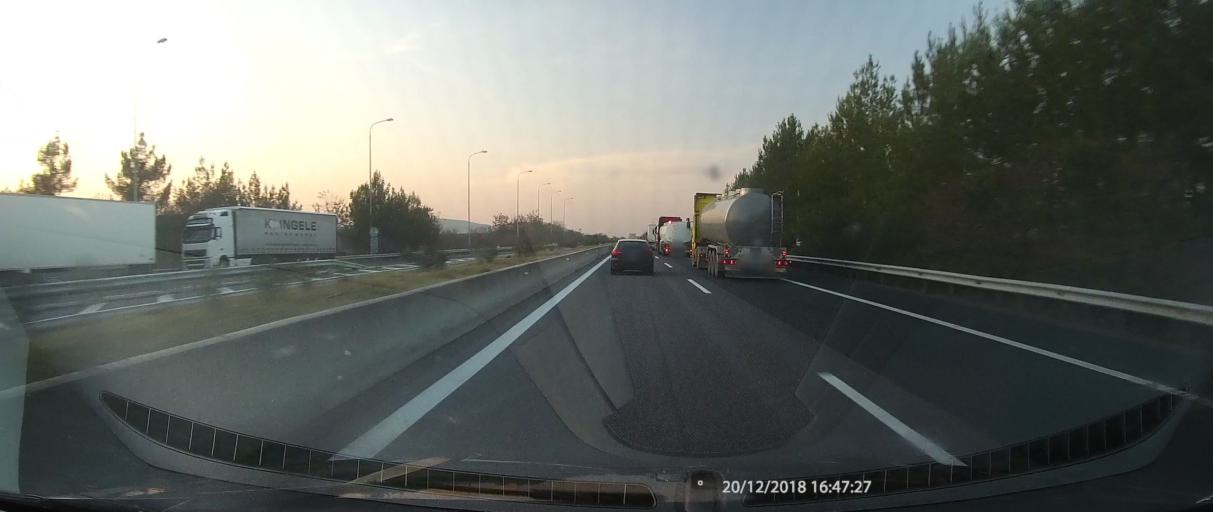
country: GR
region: Thessaly
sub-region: Nomos Magnisias
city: Stefanoviki
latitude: 39.4744
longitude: 22.6564
